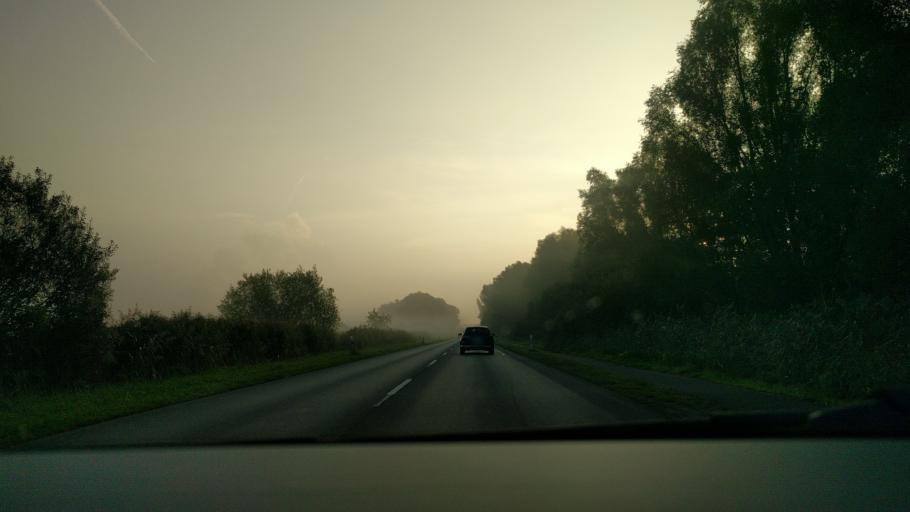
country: DE
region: Lower Saxony
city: Weyhausen
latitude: 52.4351
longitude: 10.7190
